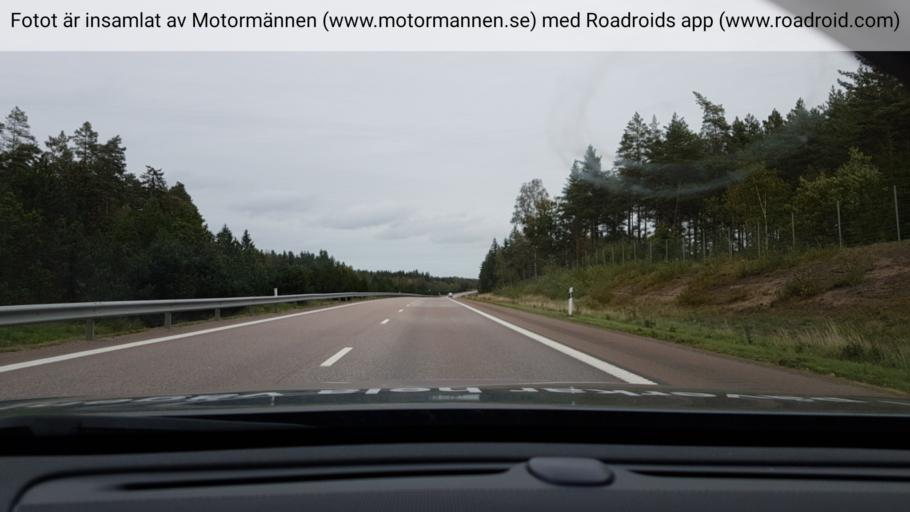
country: SE
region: OEstergoetland
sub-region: Mjolby Kommun
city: Mjolby
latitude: 58.3183
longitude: 15.0544
